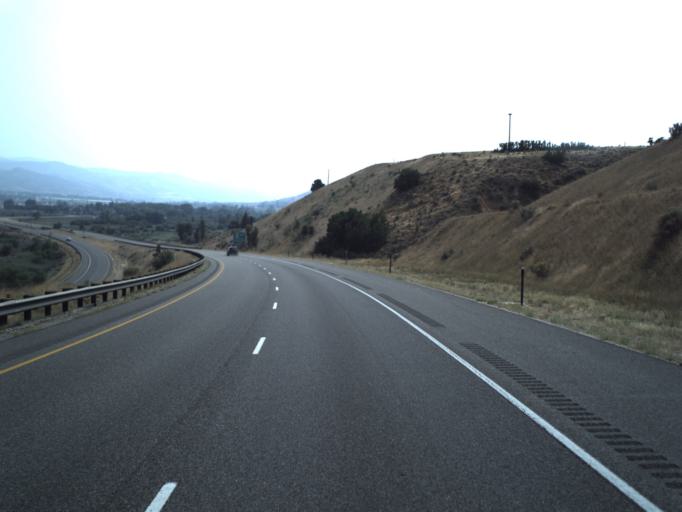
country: US
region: Utah
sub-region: Summit County
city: Coalville
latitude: 40.9244
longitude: -111.4115
